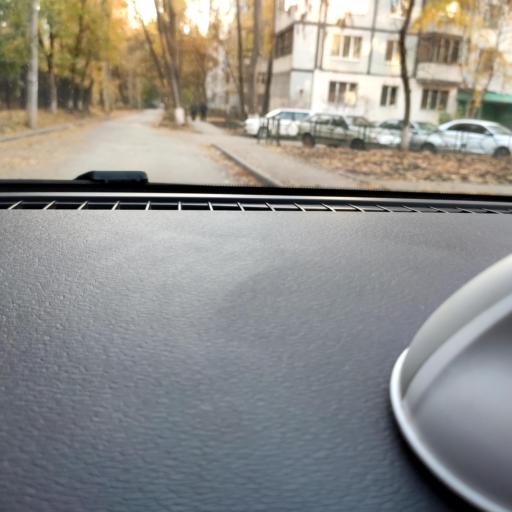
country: RU
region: Samara
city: Samara
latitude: 53.2596
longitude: 50.2295
